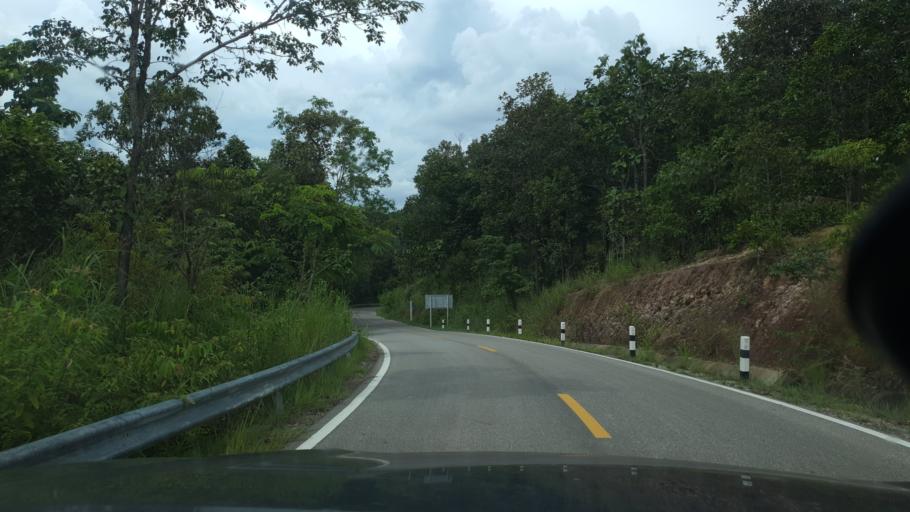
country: TH
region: Lamphun
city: Mae Tha
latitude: 18.5176
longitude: 99.2619
